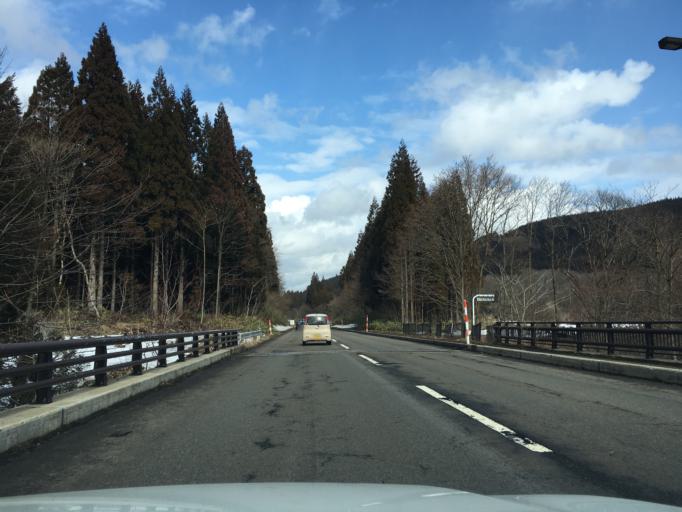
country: JP
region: Akita
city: Takanosu
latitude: 40.0100
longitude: 140.2787
